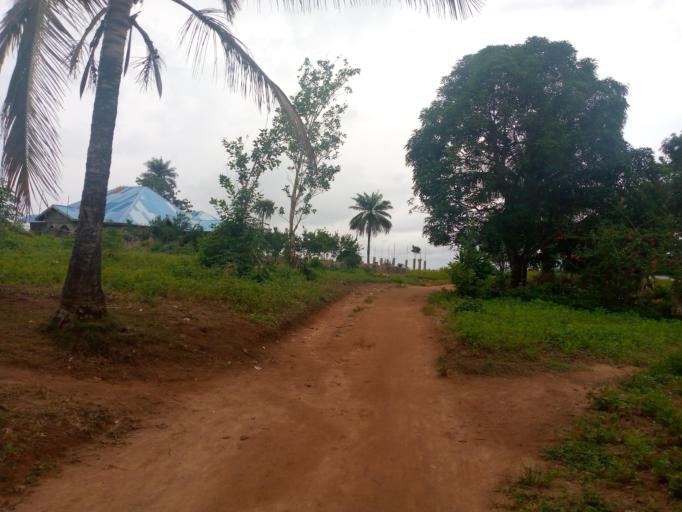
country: SL
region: Southern Province
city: Sumbuya
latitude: 7.6016
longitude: -12.1632
